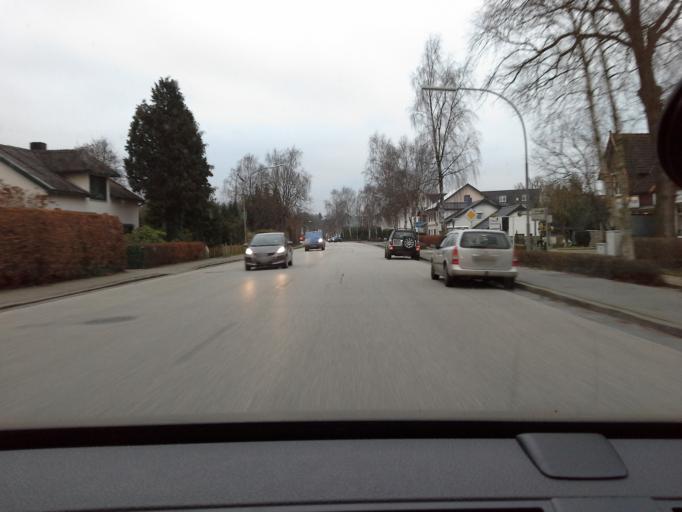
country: DE
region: Schleswig-Holstein
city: Quickborn
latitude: 53.7242
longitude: 9.9003
